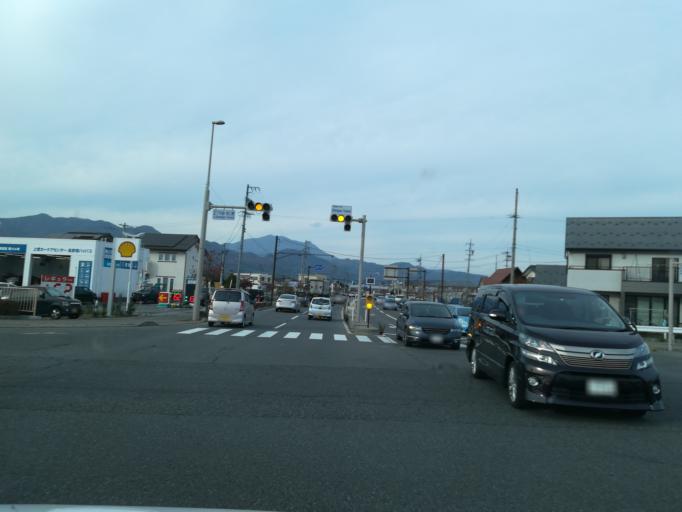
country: JP
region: Nagano
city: Nagano-shi
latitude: 36.6031
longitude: 138.1792
